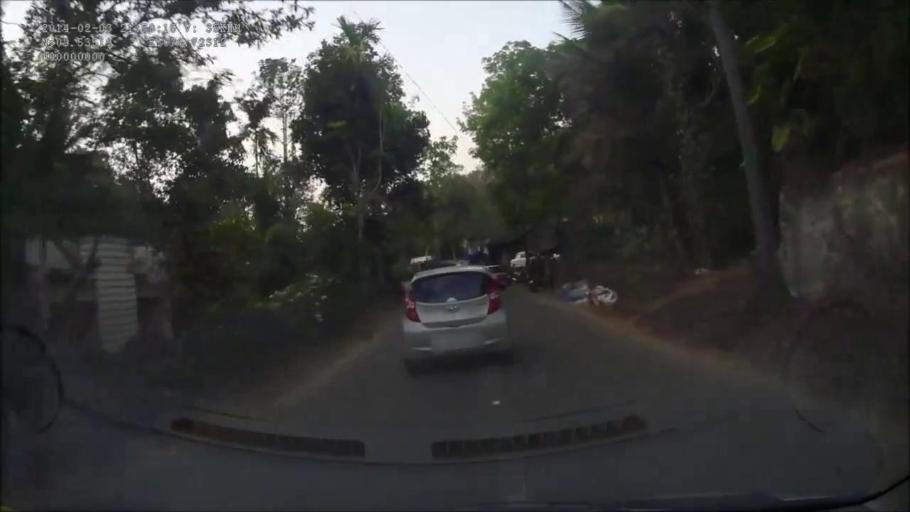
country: IN
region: Kerala
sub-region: Kottayam
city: Erattupetta
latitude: 9.5350
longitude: 76.7234
